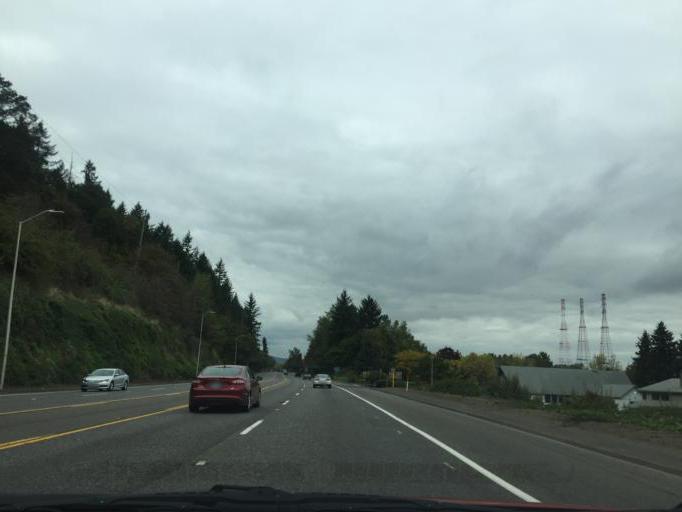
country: US
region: Oregon
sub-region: Washington County
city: Oak Hills
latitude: 45.6064
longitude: -122.7916
